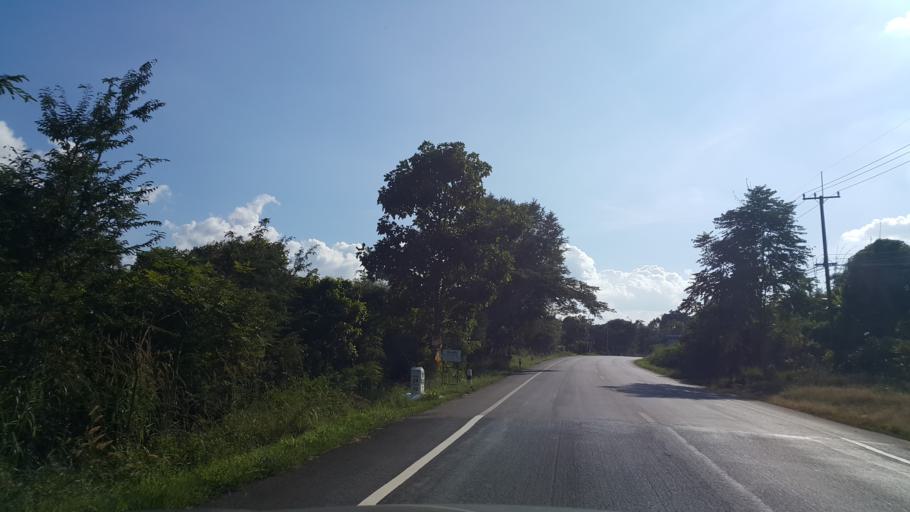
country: TH
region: Lamphun
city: Mae Tha
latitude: 18.4956
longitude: 99.1937
